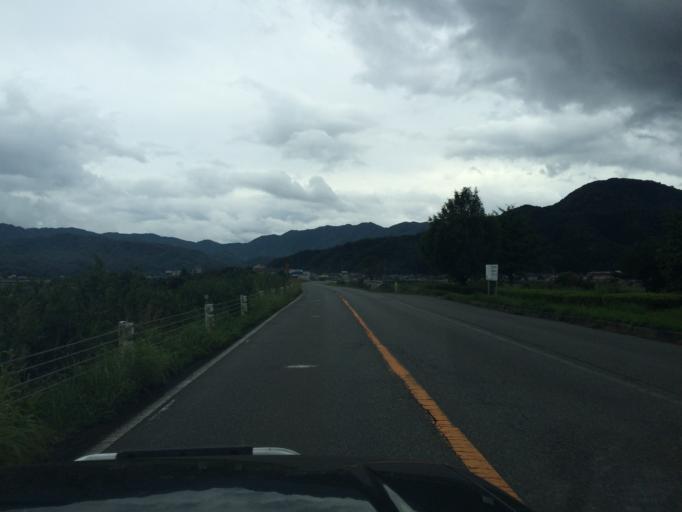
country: JP
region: Hyogo
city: Toyooka
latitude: 35.4457
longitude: 134.7734
